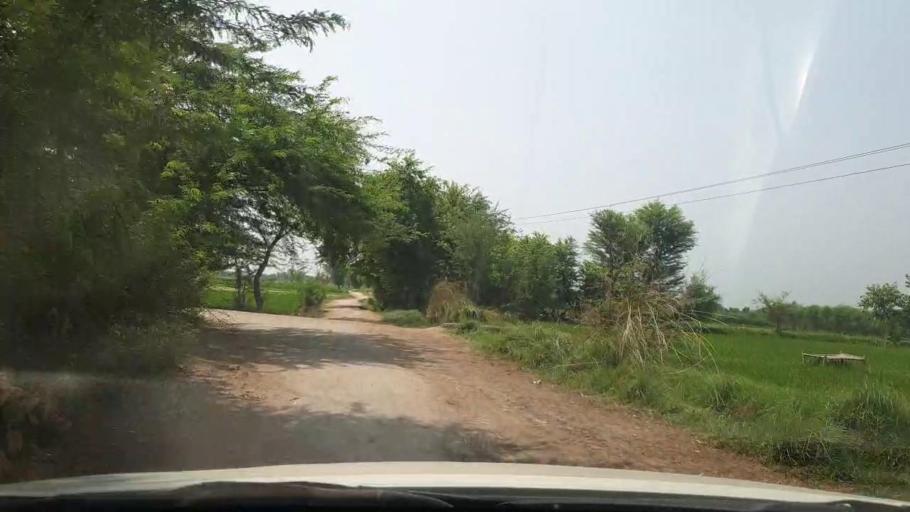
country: PK
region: Sindh
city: Shikarpur
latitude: 27.9881
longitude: 68.7133
